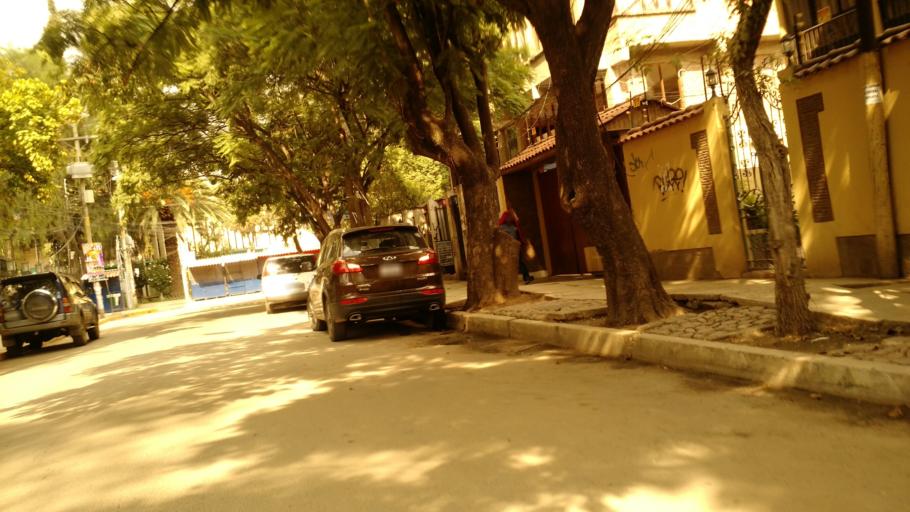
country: BO
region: Cochabamba
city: Cochabamba
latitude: -17.3950
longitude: -66.1487
